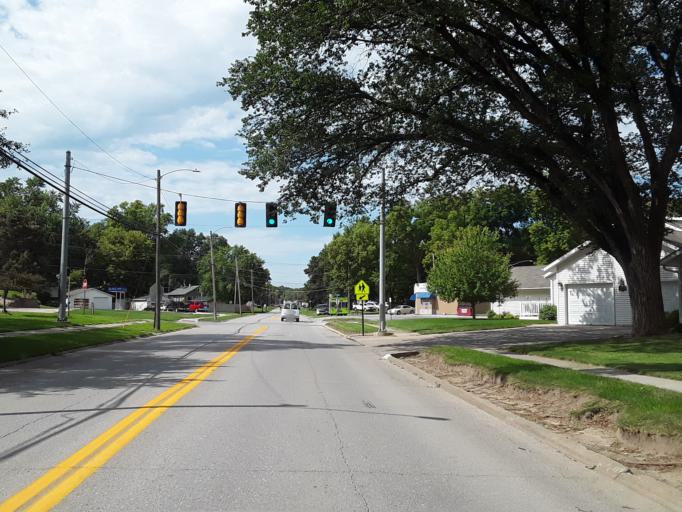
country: US
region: Nebraska
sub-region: Cass County
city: Plattsmouth
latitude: 41.0077
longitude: -95.8900
